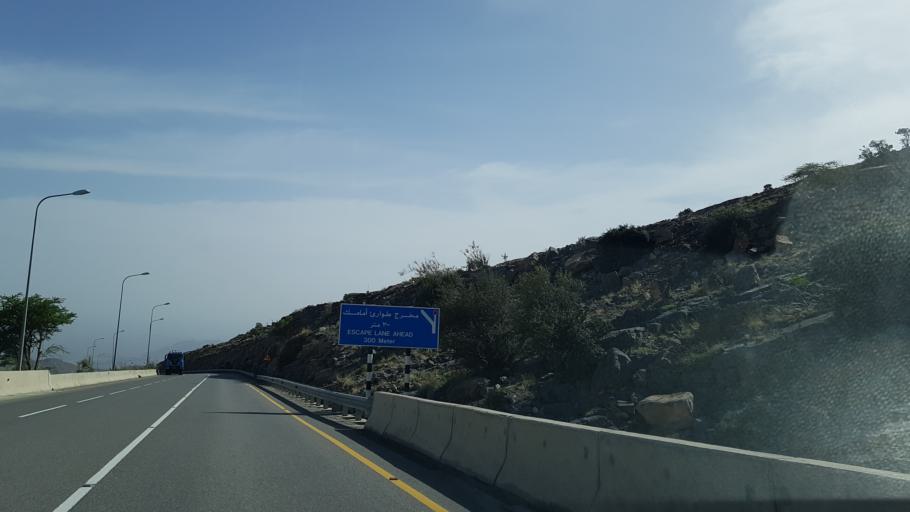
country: OM
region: Muhafazat ad Dakhiliyah
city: Izki
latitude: 23.0084
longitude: 57.6989
